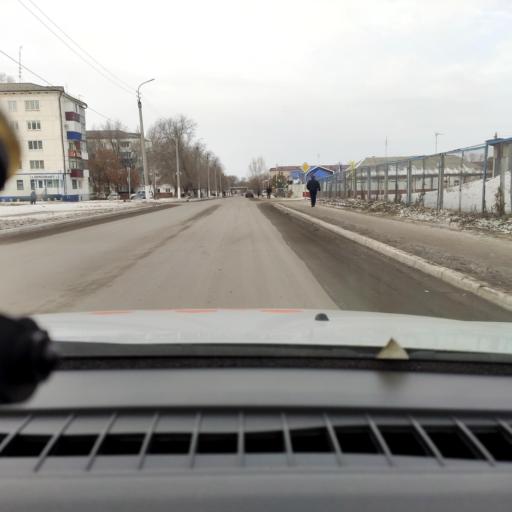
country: RU
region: Samara
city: Chapayevsk
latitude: 52.9586
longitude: 49.6901
